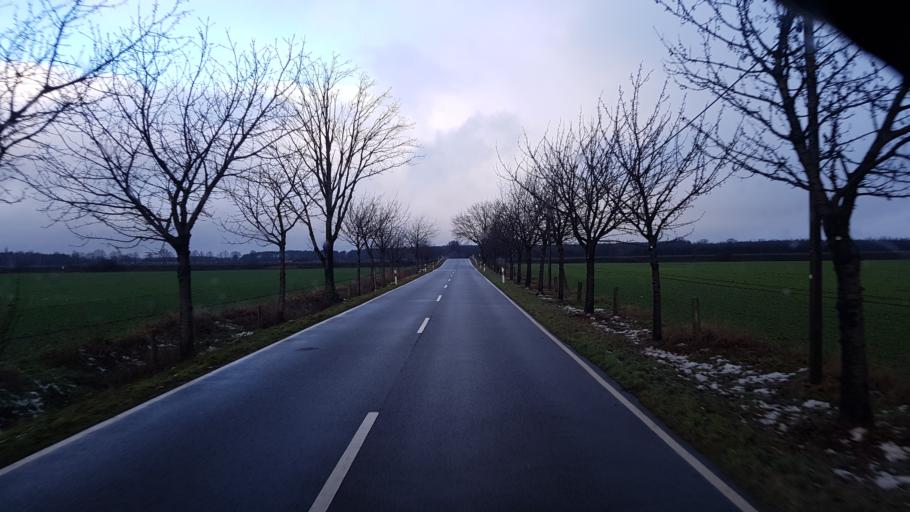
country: DE
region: Brandenburg
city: Heinersbruck
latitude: 51.8273
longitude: 14.5068
